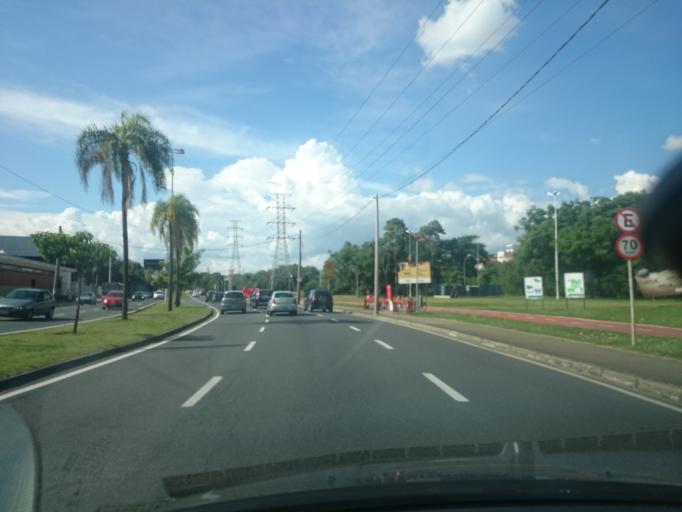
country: BR
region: Sao Paulo
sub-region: Sorocaba
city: Sorocaba
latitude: -23.5064
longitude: -47.4518
